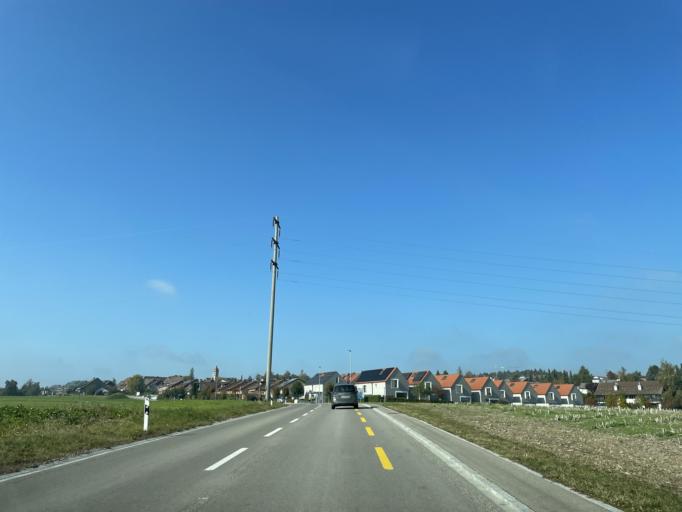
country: CH
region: Zurich
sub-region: Bezirk Winterthur
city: Brutten
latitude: 47.4707
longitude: 8.6846
